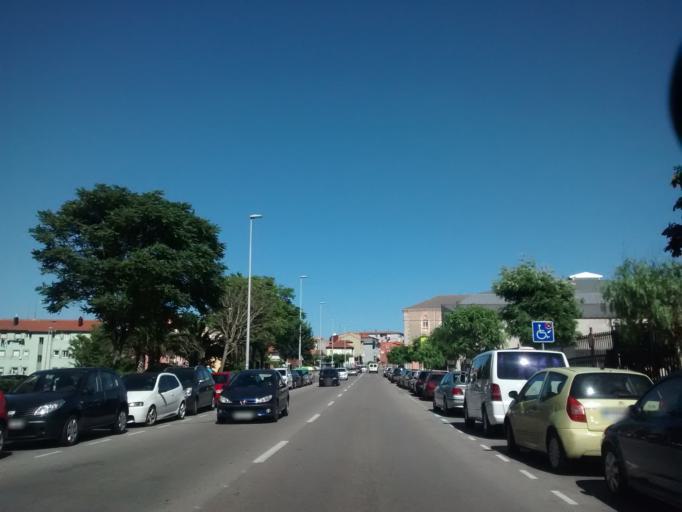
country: ES
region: Cantabria
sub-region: Provincia de Cantabria
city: Santander
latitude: 43.4676
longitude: -3.8119
